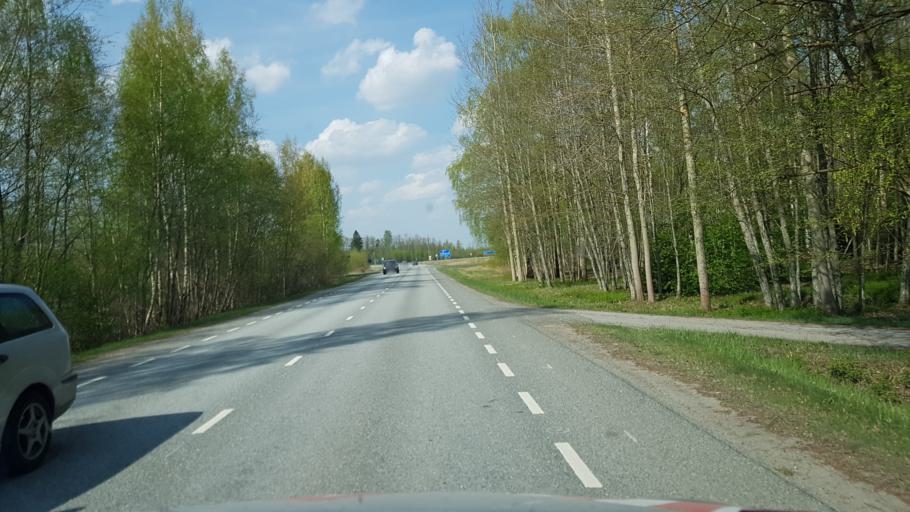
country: EE
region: Paernumaa
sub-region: Sindi linn
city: Sindi
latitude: 58.4191
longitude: 24.6706
